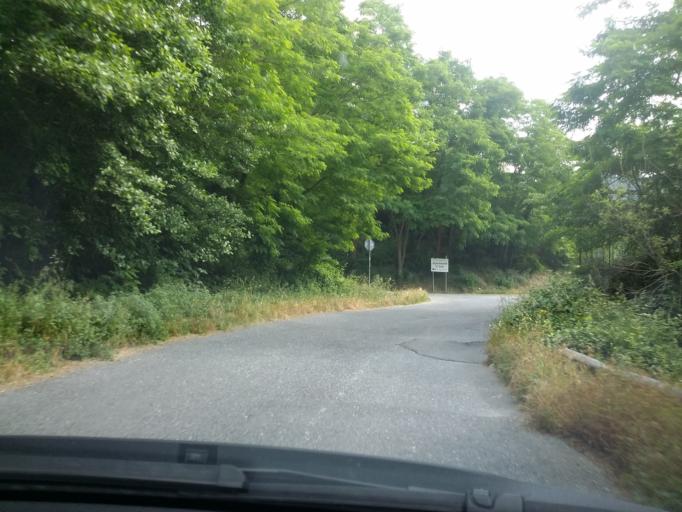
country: IT
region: Liguria
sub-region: Provincia di Savona
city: Orco Feglino
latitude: 44.2232
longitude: 8.3275
